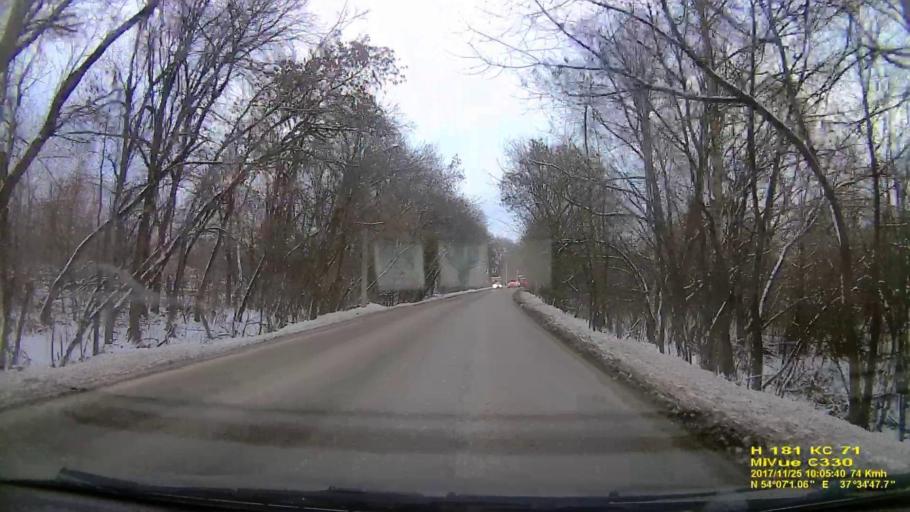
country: RU
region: Tula
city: Mendeleyevskiy
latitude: 54.1169
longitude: 37.5803
